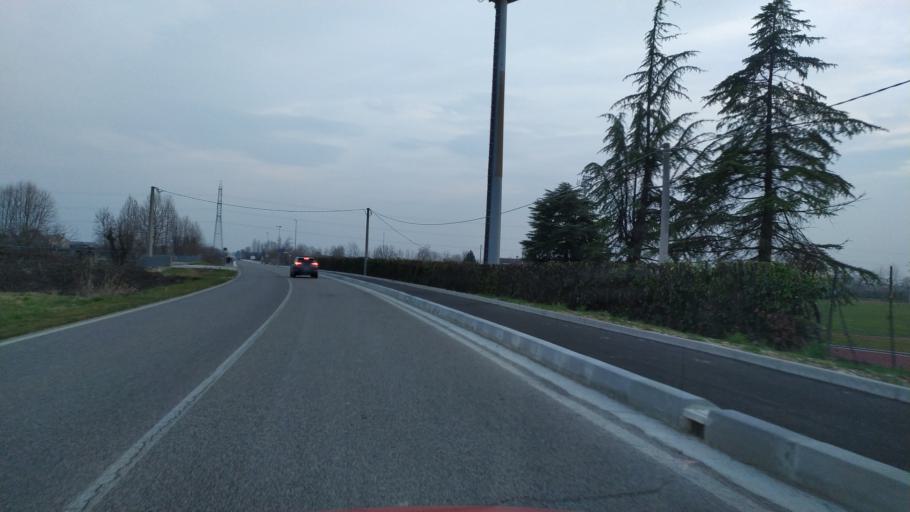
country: IT
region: Veneto
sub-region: Provincia di Vicenza
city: Dueville
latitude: 45.6342
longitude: 11.5576
